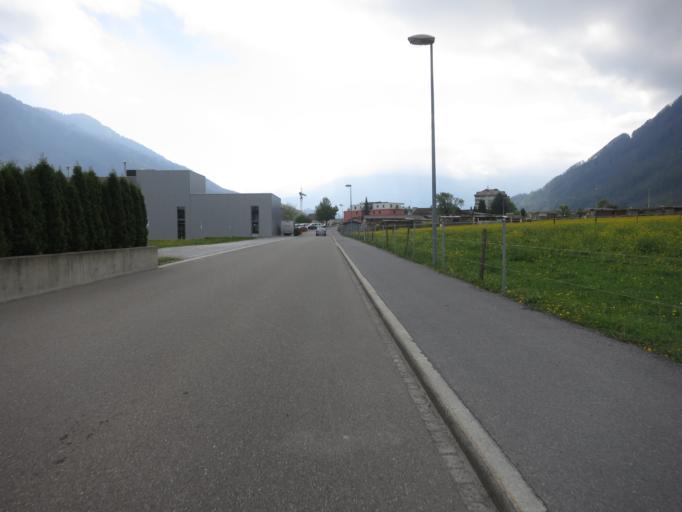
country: CH
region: Glarus
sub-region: Glarus
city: Bilten
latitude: 47.1541
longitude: 9.0226
